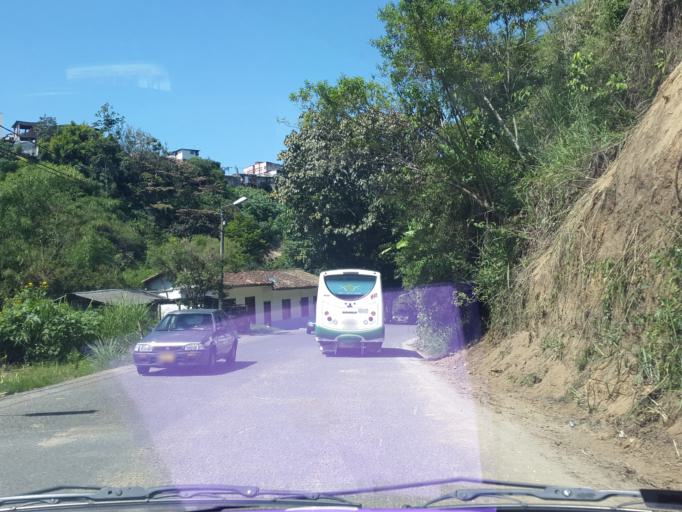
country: CO
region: Quindio
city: Armenia
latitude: 4.5316
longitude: -75.6691
